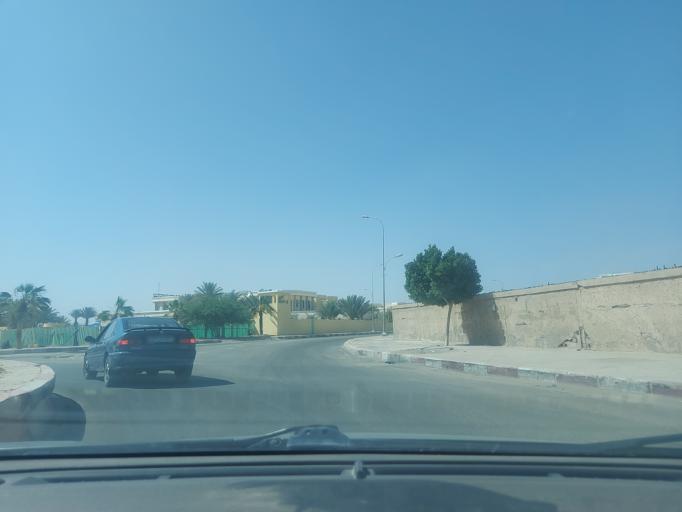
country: MR
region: Nouakchott
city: Nouakchott
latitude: 18.0990
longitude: -15.9586
